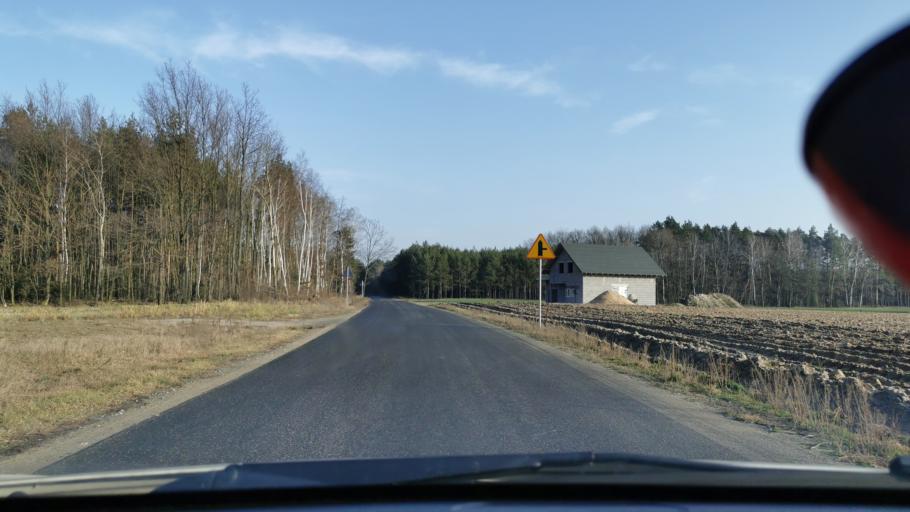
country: PL
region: Greater Poland Voivodeship
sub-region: Powiat kaliski
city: Opatowek
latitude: 51.6602
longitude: 18.2573
